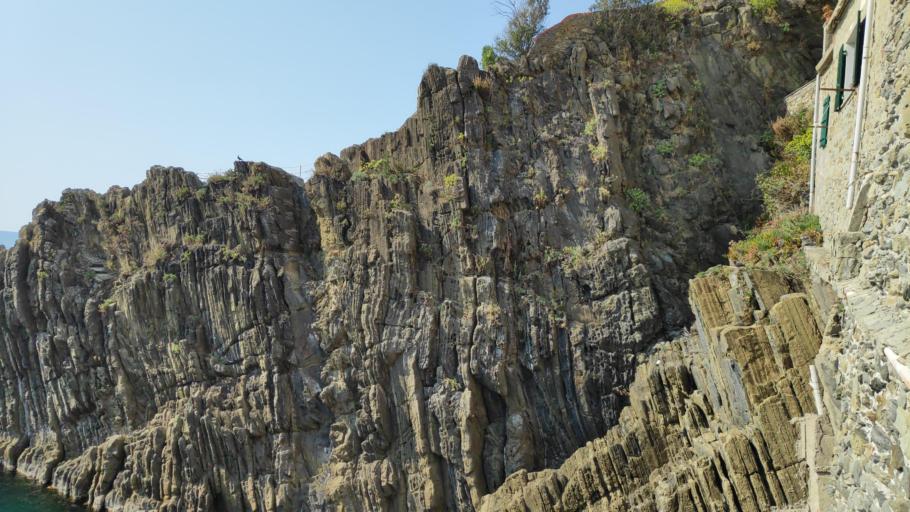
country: IT
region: Liguria
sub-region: Provincia di La Spezia
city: Riomaggiore
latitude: 44.0987
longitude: 9.7374
